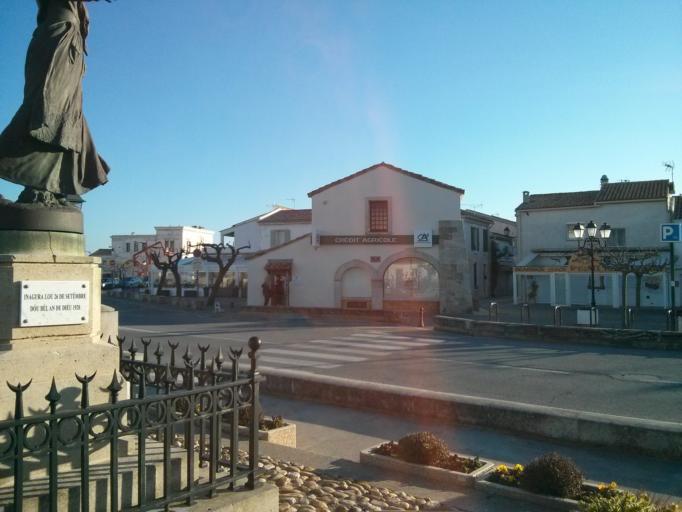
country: FR
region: Provence-Alpes-Cote d'Azur
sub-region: Departement des Bouches-du-Rhone
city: Saintes-Maries-de-la-Mer
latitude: 43.4523
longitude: 4.4285
